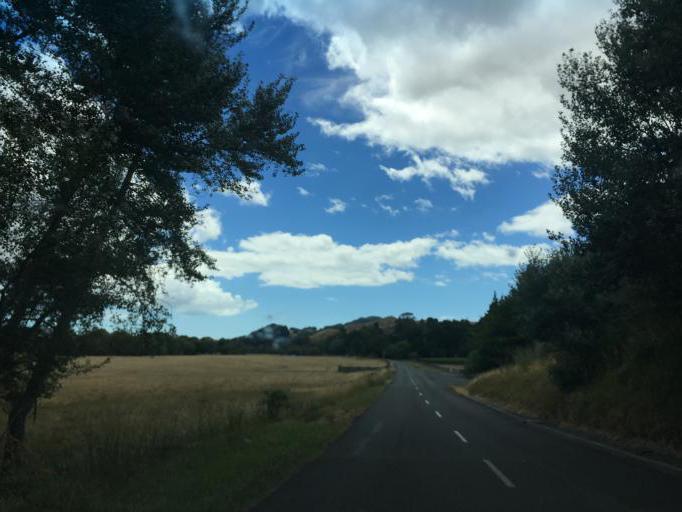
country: NZ
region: Hawke's Bay
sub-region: Hastings District
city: Hastings
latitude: -39.7338
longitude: 176.9075
